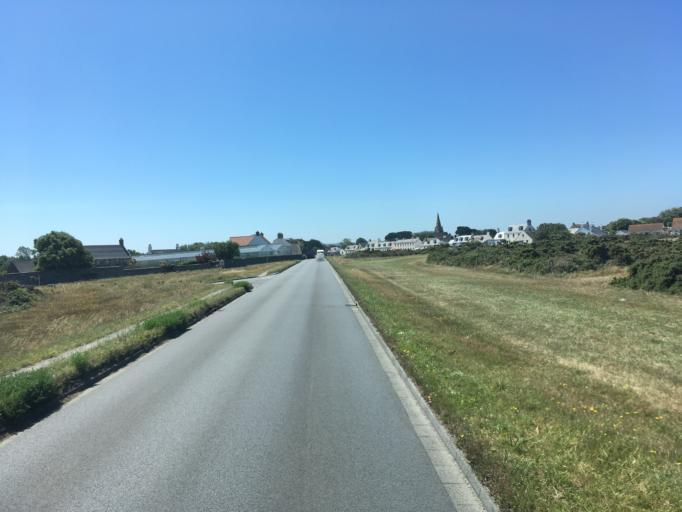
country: GG
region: St Peter Port
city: Saint Peter Port
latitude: 49.4967
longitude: -2.5355
